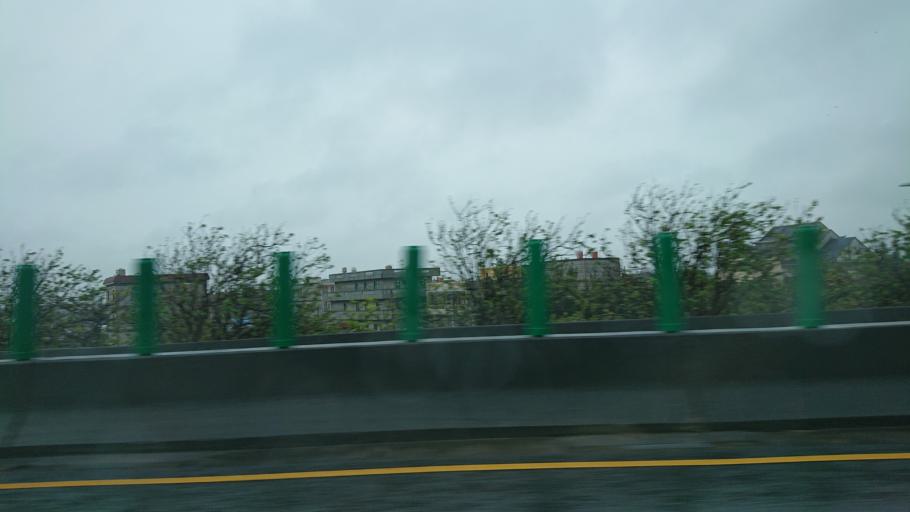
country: TW
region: Taiwan
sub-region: Chiayi
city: Taibao
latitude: 23.7169
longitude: 120.2070
